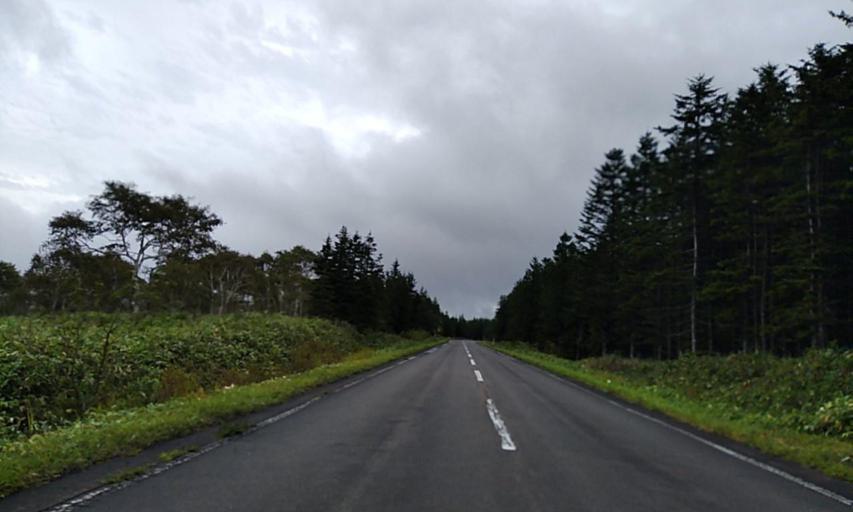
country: JP
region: Hokkaido
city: Abashiri
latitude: 43.6130
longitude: 144.5907
